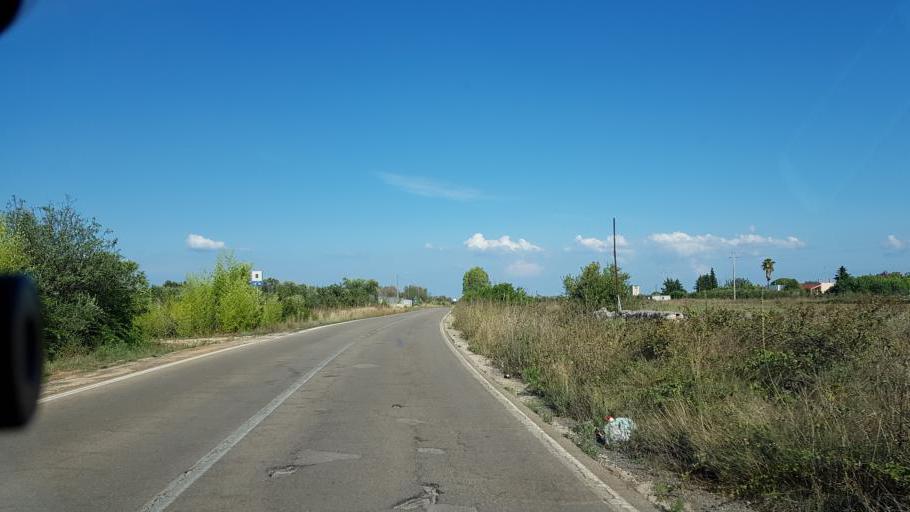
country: IT
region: Apulia
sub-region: Provincia di Lecce
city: Monteroni di Lecce
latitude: 40.2911
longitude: 18.0858
